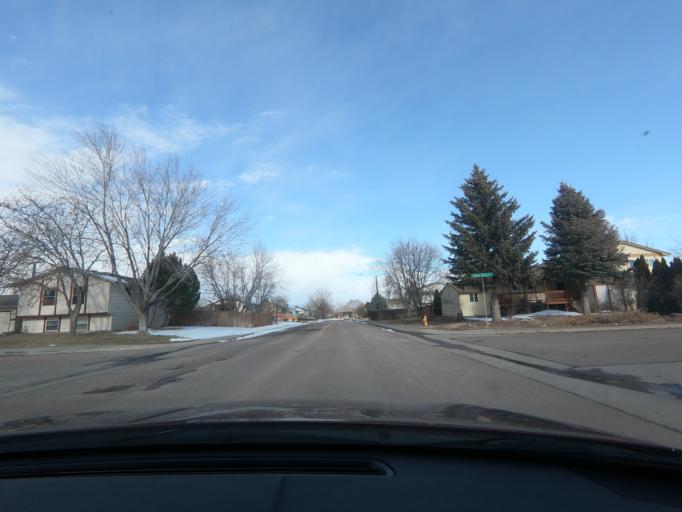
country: US
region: Colorado
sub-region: El Paso County
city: Security-Widefield
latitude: 38.7335
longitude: -104.6877
